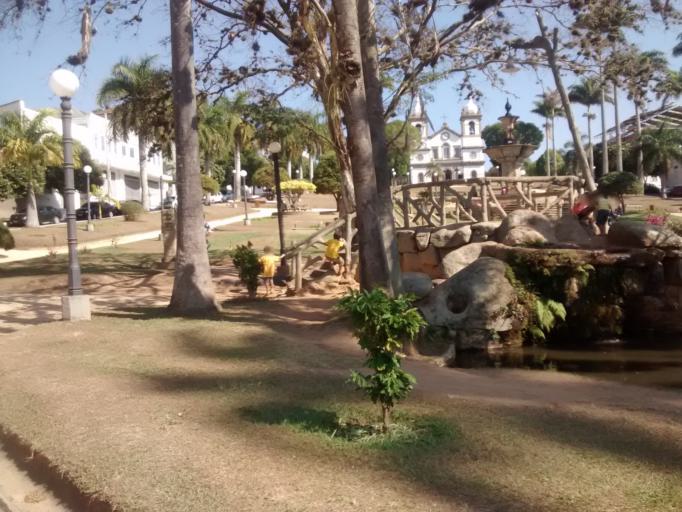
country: BR
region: Rio de Janeiro
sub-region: Vassouras
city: Vassouras
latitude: -22.4091
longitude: -43.6607
